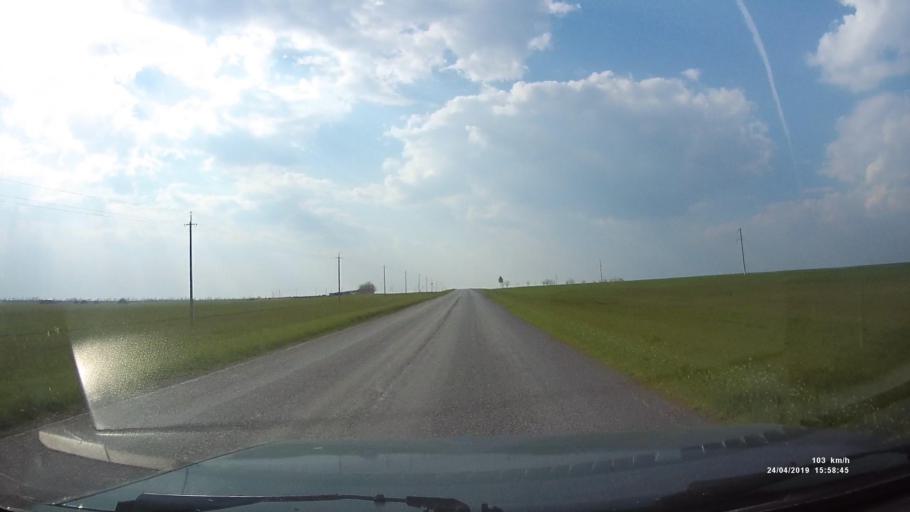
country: RU
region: Kalmykiya
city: Yashalta
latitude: 46.6171
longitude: 42.4844
